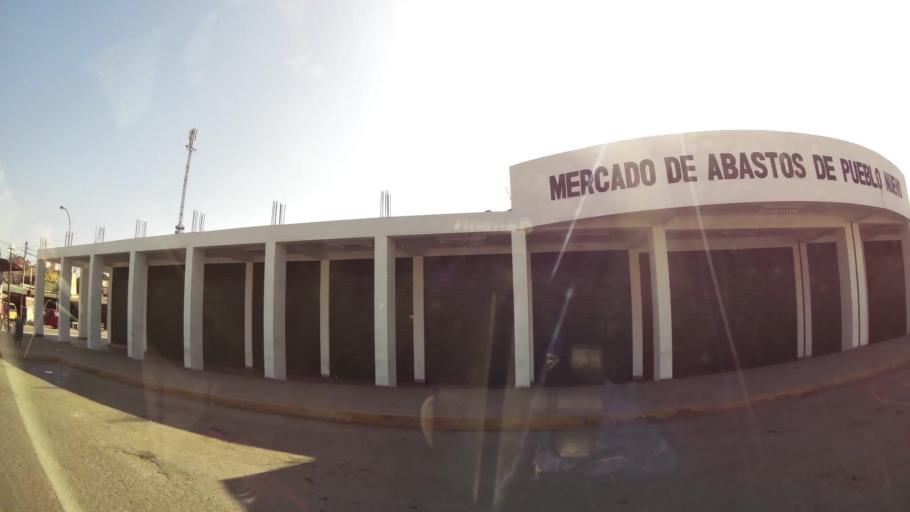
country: PE
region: Ica
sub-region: Provincia de Chincha
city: Chincha Alta
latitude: -13.4022
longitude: -76.1292
